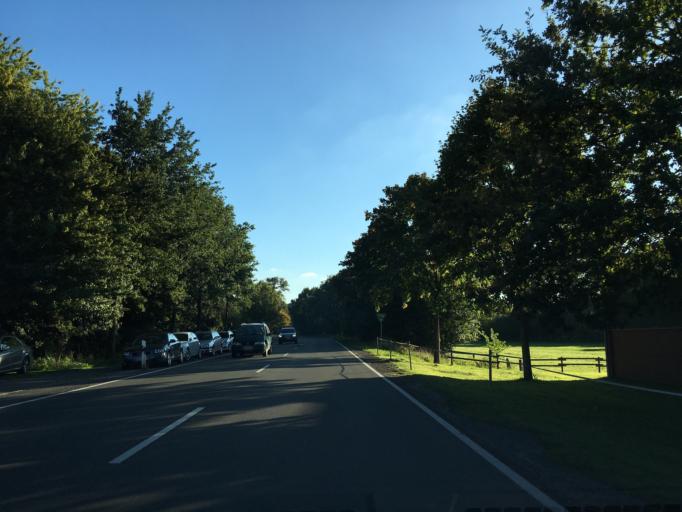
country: DE
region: North Rhine-Westphalia
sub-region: Regierungsbezirk Munster
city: Greven
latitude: 52.0189
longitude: 7.5601
